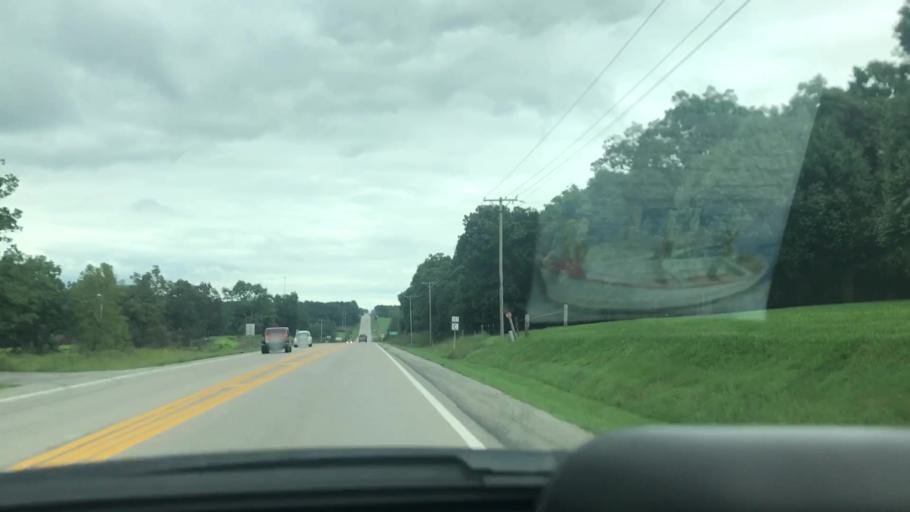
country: US
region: Missouri
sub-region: Dallas County
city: Buffalo
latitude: 37.6742
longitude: -93.1032
